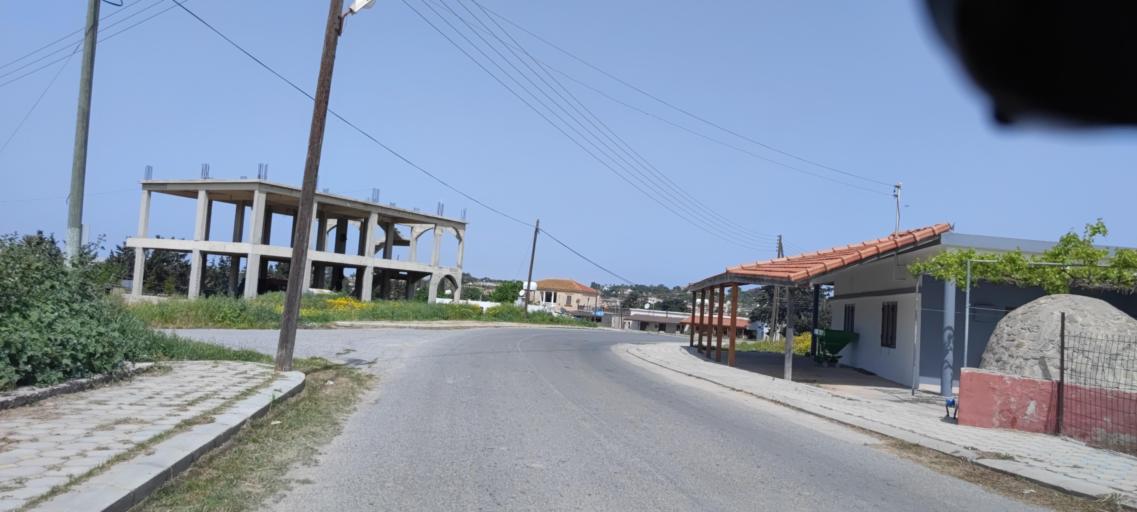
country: CY
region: Ammochostos
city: Rizokarpaso
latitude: 35.5924
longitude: 34.3857
